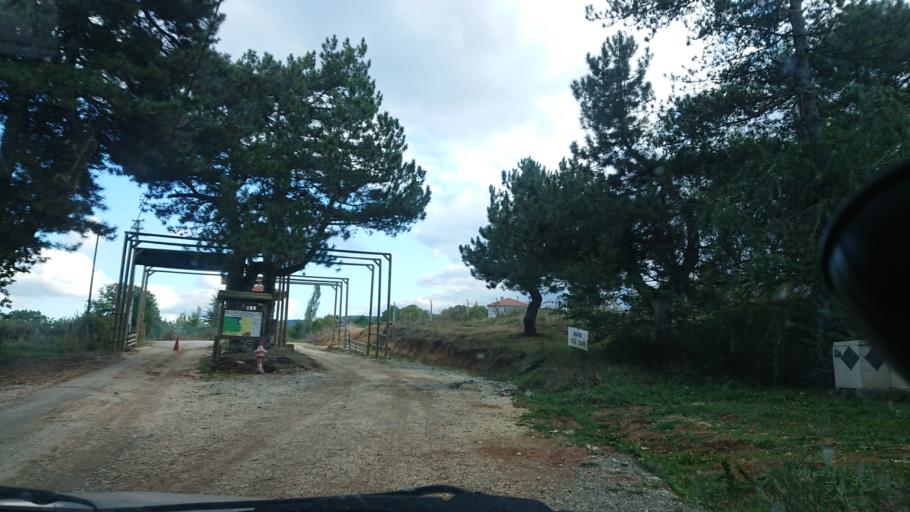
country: TR
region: Bilecik
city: Pazaryeri
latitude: 40.0123
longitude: 29.7977
